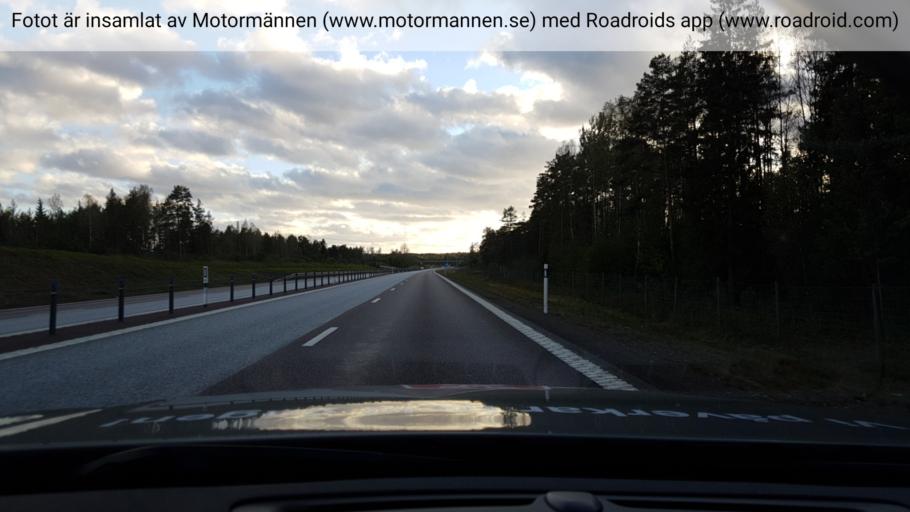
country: SE
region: Vaermland
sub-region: Karlstads Kommun
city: Skattkarr
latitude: 59.4152
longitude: 13.6625
